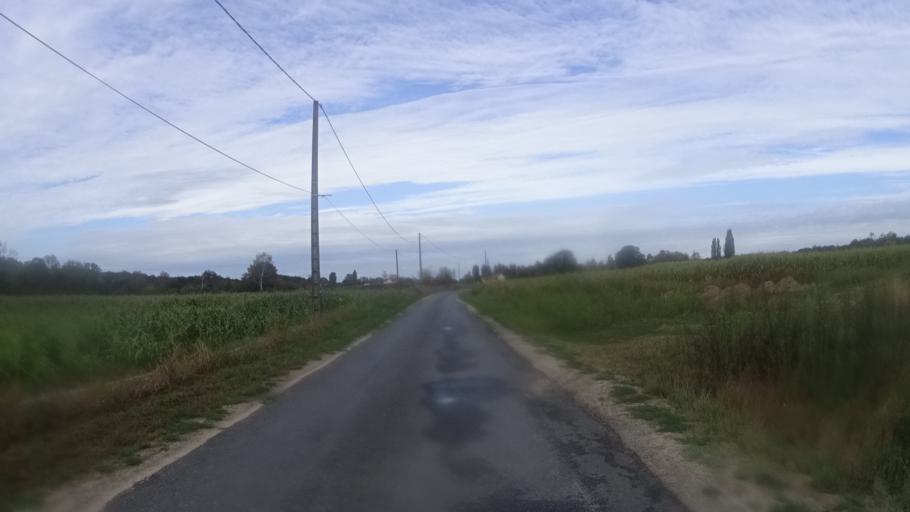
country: FR
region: Centre
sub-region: Departement du Loiret
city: Fay-aux-Loges
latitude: 47.9376
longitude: 2.1878
